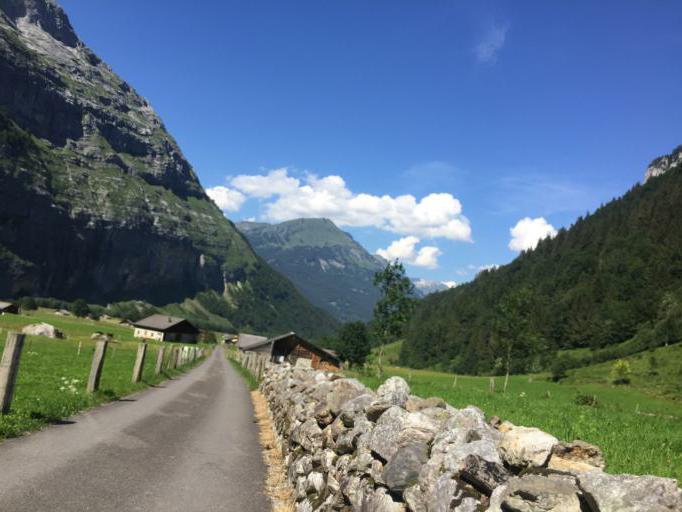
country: CH
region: Bern
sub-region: Interlaken-Oberhasli District
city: Meiringen
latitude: 46.6747
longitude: 8.2071
